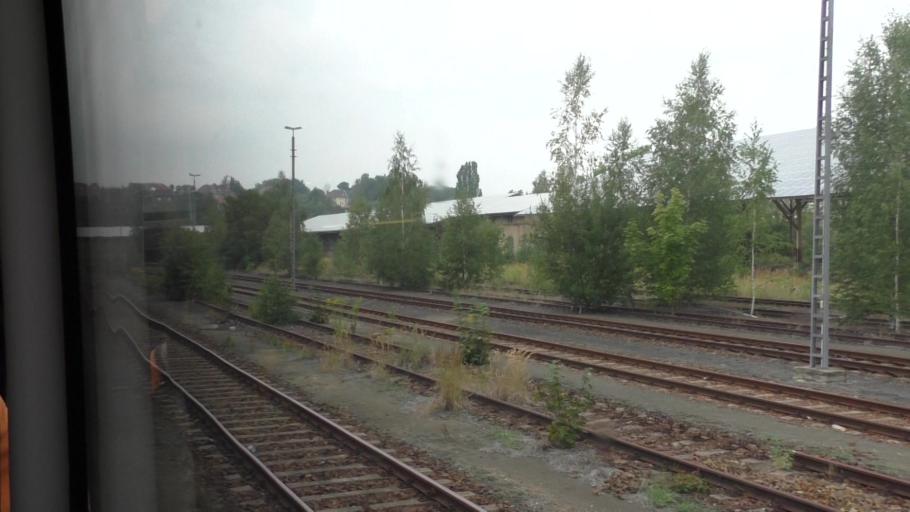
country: DE
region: Saxony
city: Zittau
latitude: 50.9045
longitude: 14.8068
